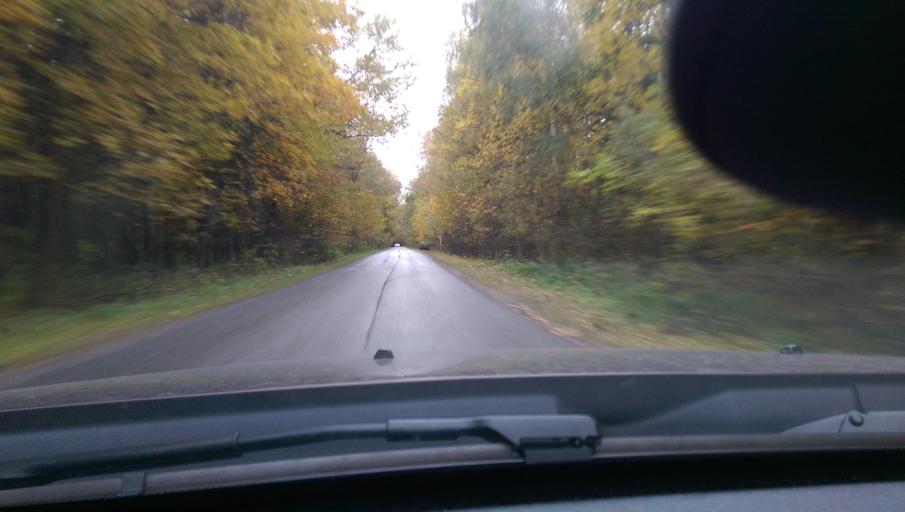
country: RU
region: Moskovskaya
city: Pirogovskiy
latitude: 56.0221
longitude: 37.7190
